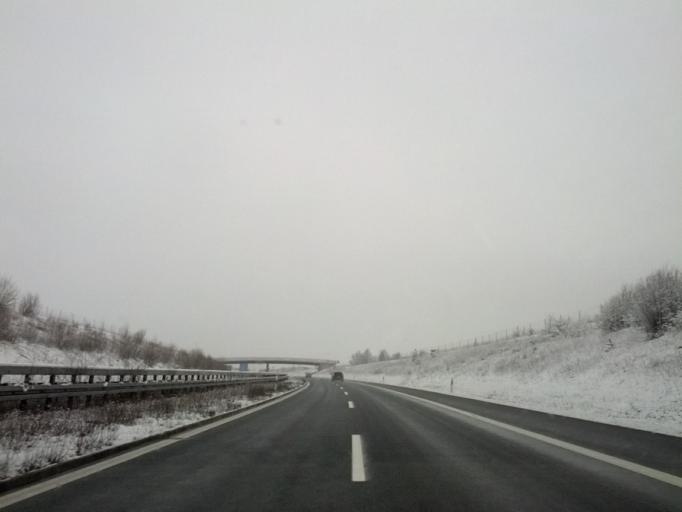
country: DE
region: Bavaria
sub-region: Regierungsbezirk Unterfranken
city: Geldersheim
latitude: 50.0498
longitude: 10.1472
